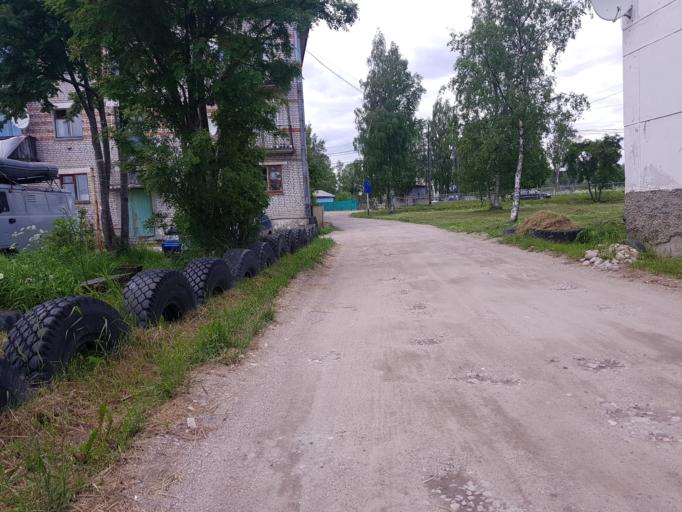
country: RU
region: Republic of Karelia
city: Kalevala
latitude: 65.1959
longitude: 31.1994
